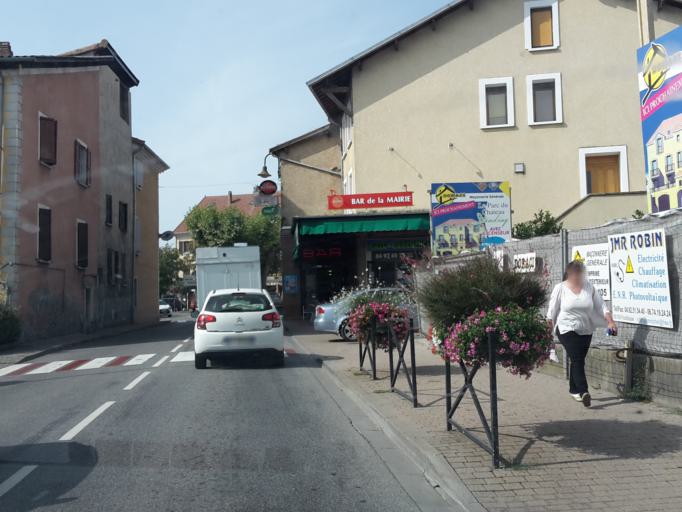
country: FR
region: Provence-Alpes-Cote d'Azur
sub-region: Departement des Hautes-Alpes
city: Tallard
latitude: 44.4624
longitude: 6.0556
